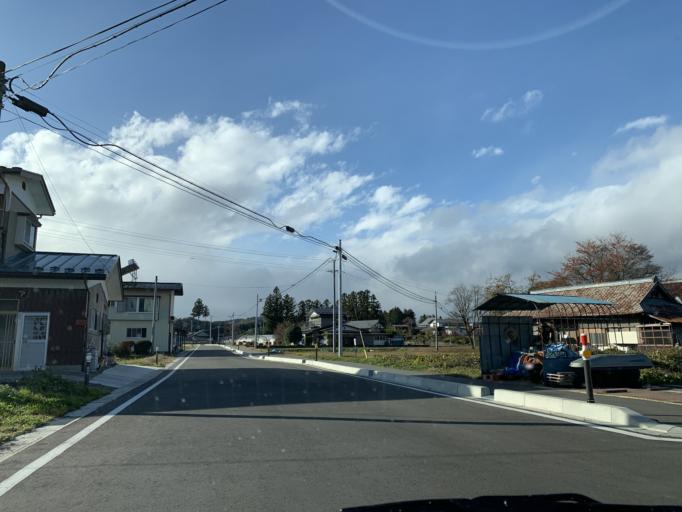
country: JP
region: Iwate
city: Ichinoseki
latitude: 39.0078
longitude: 141.0999
